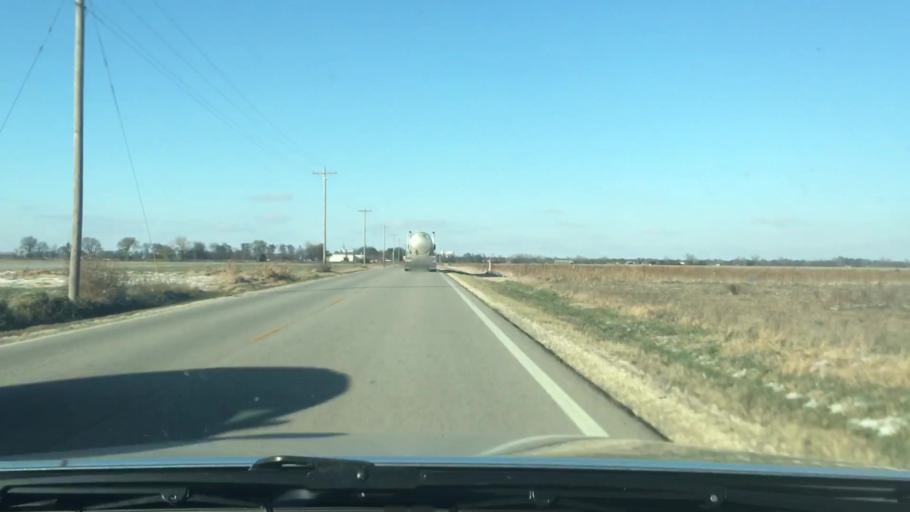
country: US
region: Kansas
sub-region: Rice County
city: Sterling
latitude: 38.1804
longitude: -98.2069
